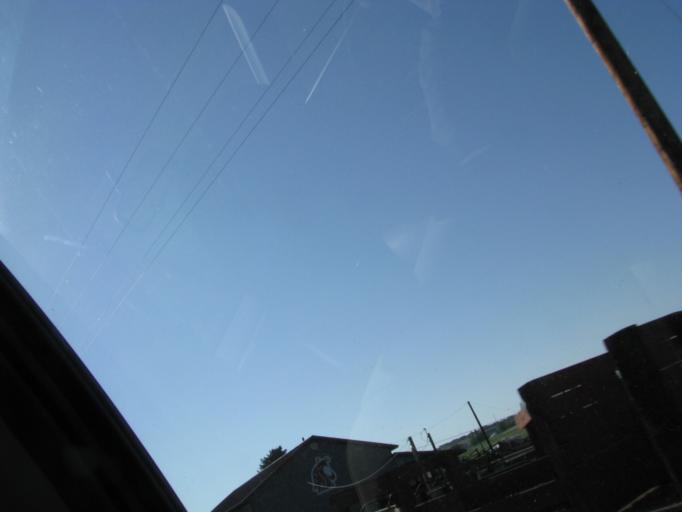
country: US
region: Washington
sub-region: Spokane County
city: Liberty Lake
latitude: 47.6277
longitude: -117.1474
